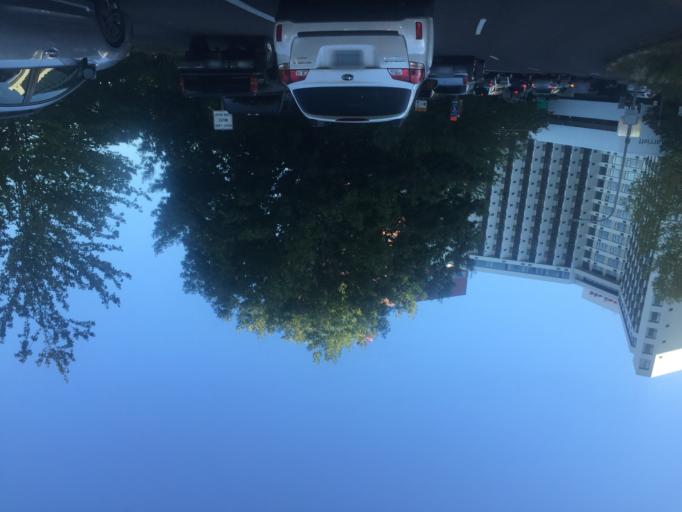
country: US
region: Oregon
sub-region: Multnomah County
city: Portland
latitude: 45.5116
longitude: -122.6750
